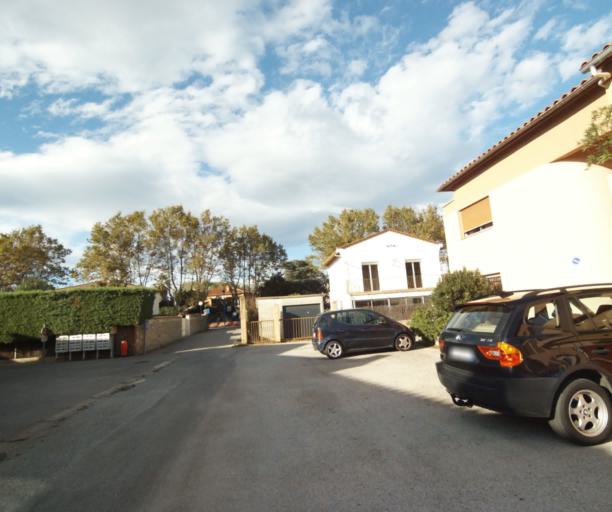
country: FR
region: Languedoc-Roussillon
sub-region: Departement des Pyrenees-Orientales
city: Argelers
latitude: 42.5496
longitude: 3.0360
